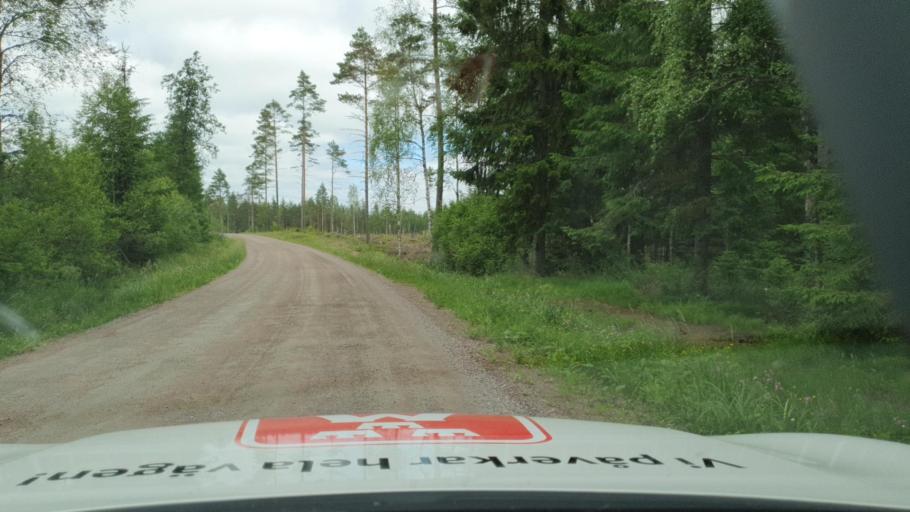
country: SE
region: Vaermland
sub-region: Filipstads Kommun
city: Filipstad
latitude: 59.6104
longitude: 13.9971
